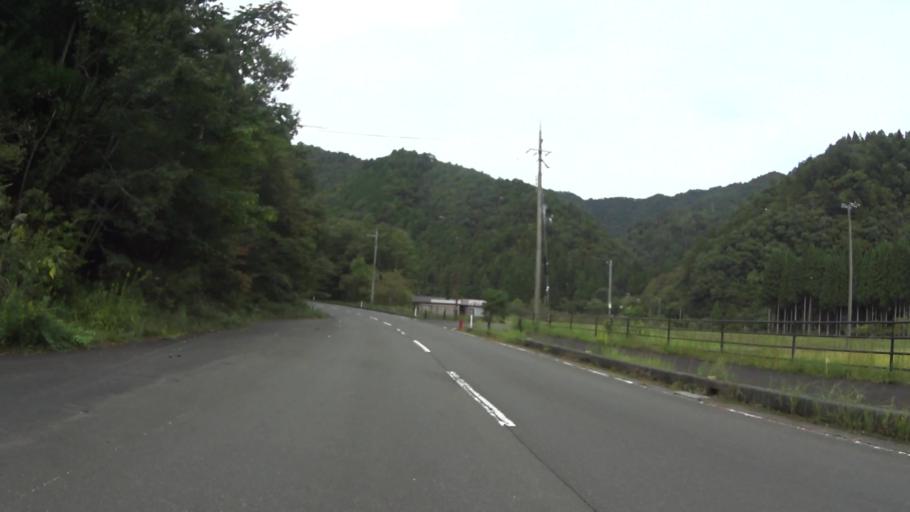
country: JP
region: Fukui
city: Obama
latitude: 35.3246
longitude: 135.6751
